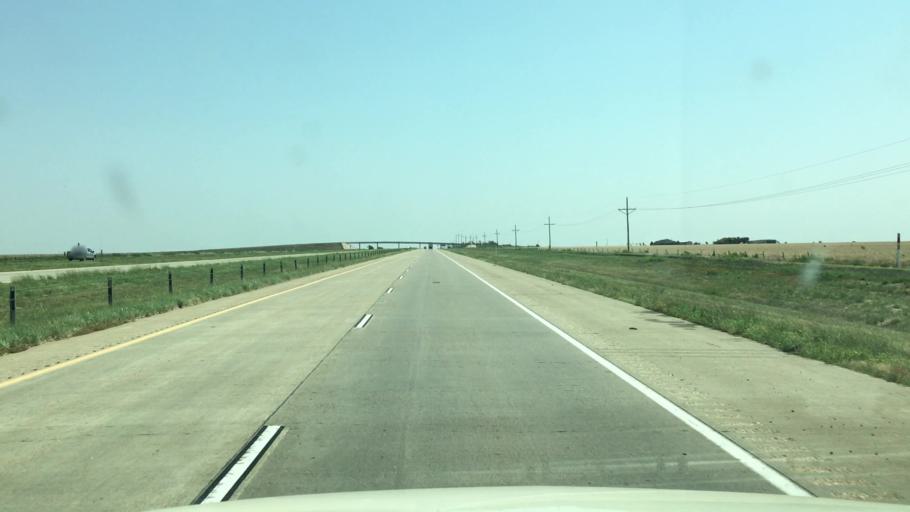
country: US
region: Texas
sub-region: Potter County
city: Bushland
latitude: 35.2071
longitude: -102.1612
